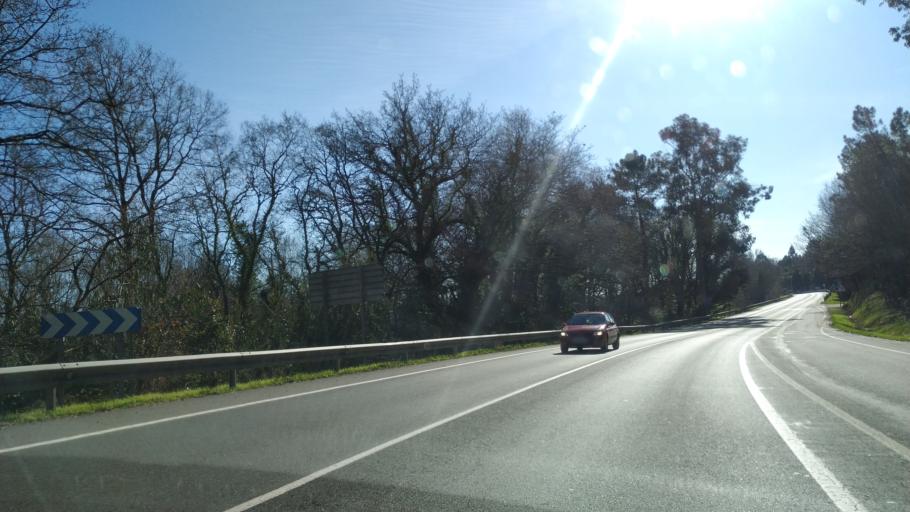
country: ES
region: Galicia
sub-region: Provincia de Pontevedra
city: Silleda
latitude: 42.6900
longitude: -8.2215
